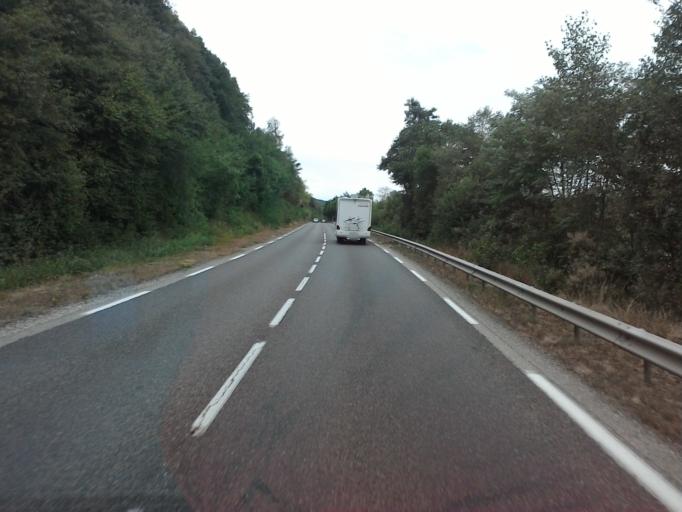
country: FR
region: Rhone-Alpes
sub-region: Departement de l'Ain
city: Sault-Brenaz
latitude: 45.8472
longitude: 5.4131
